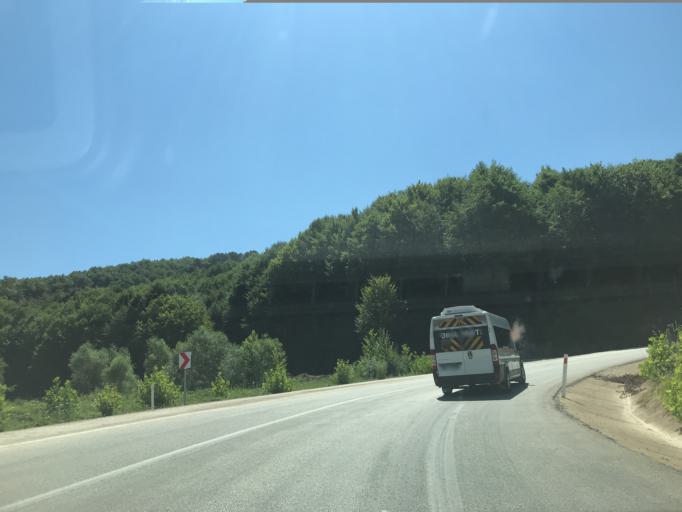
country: TR
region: Bursa
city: Tahtakopru
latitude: 39.9429
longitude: 29.6002
